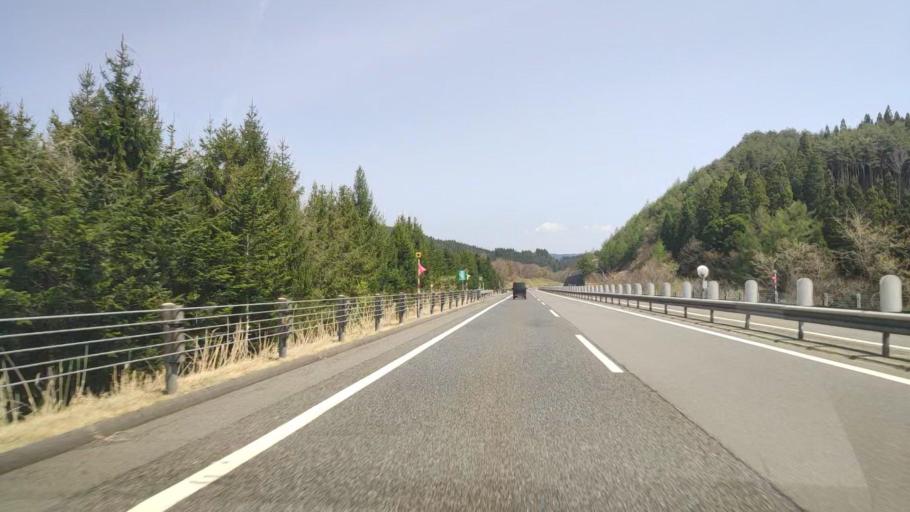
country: JP
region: Iwate
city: Ichinohe
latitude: 40.1302
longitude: 141.1026
